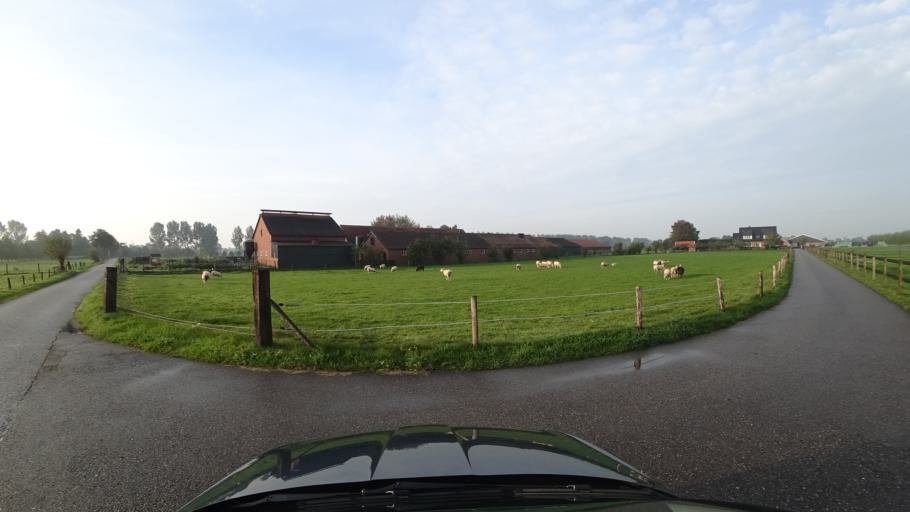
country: NL
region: Gelderland
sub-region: Gemeente Ede
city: Ede
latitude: 52.0174
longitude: 5.6168
